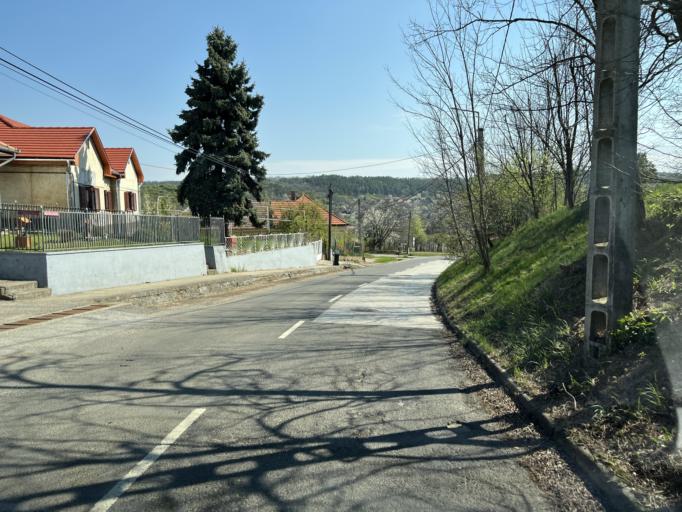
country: HU
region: Pest
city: Orbottyan
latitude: 47.7401
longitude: 19.3090
